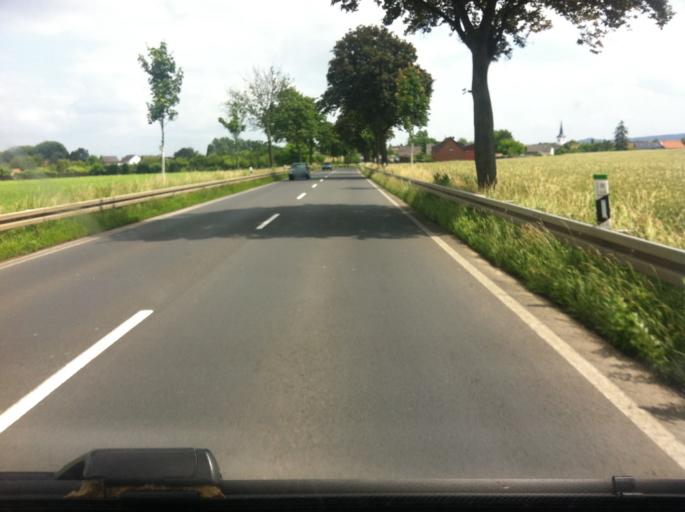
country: DE
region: North Rhine-Westphalia
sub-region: Regierungsbezirk Koln
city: Rheinbach
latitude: 50.6448
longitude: 6.9147
